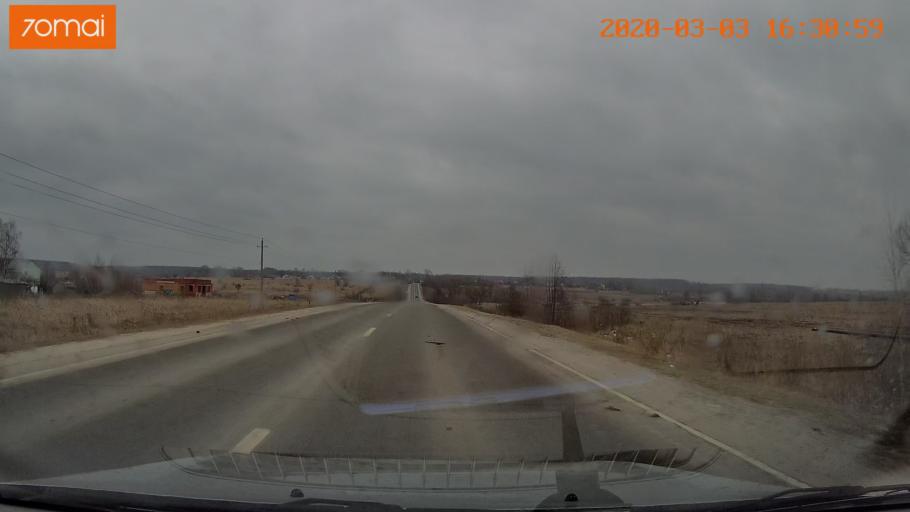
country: RU
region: Moskovskaya
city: Konobeyevo
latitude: 55.4293
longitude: 38.7176
